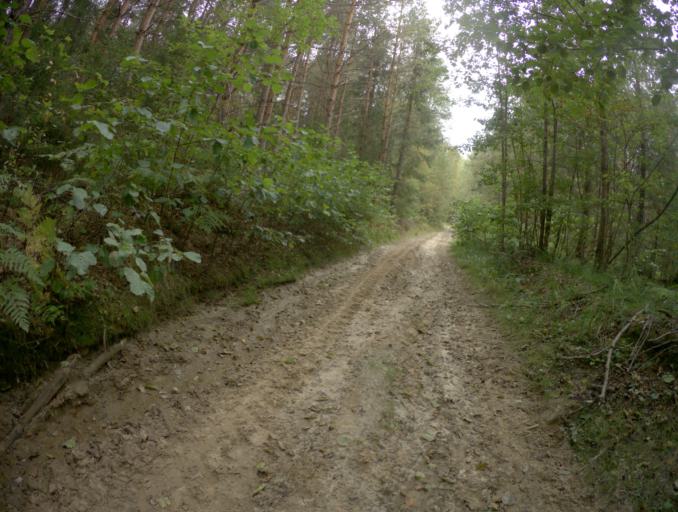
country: RU
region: Vladimir
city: Urshel'skiy
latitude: 55.8157
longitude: 40.2585
